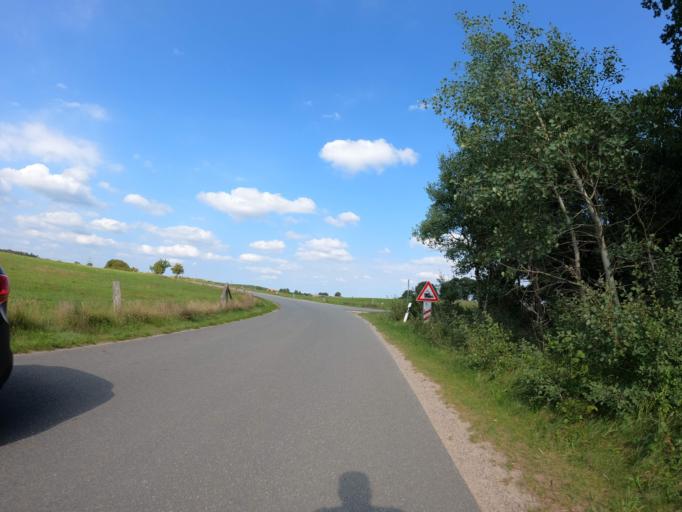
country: DE
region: Mecklenburg-Vorpommern
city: Malchow
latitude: 53.5133
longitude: 12.4426
